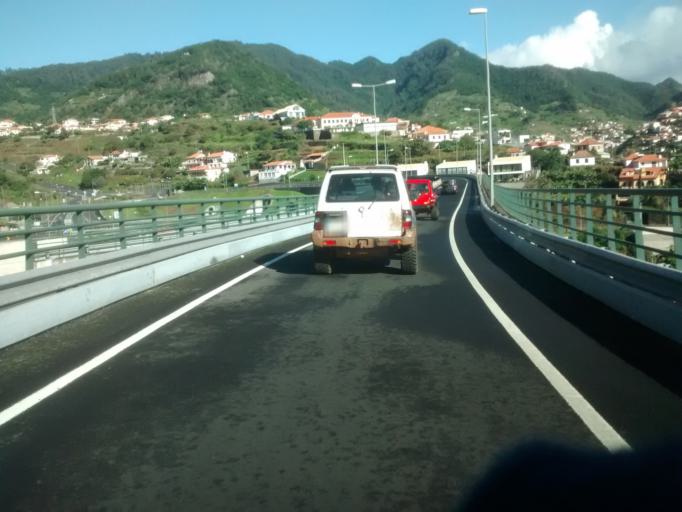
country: PT
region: Madeira
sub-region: Machico
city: Machico
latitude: 32.7274
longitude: -16.7789
